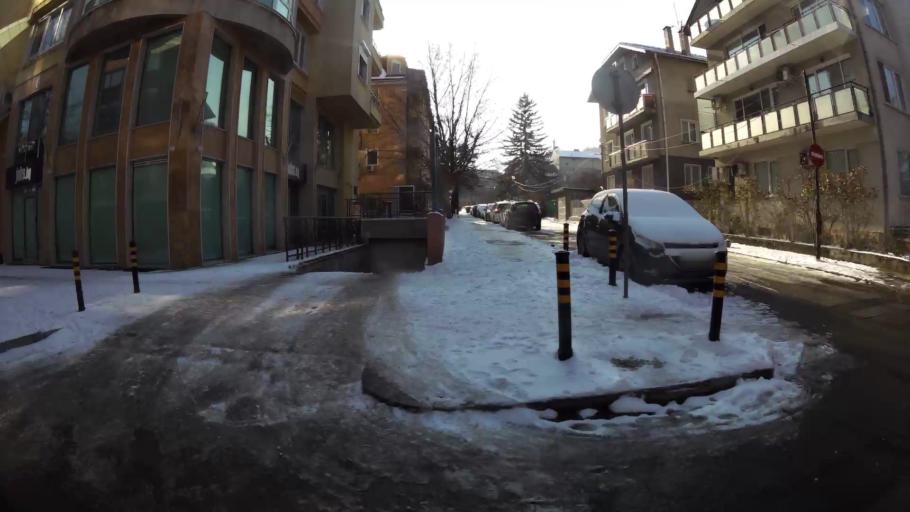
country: BG
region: Sofia-Capital
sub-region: Stolichna Obshtina
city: Sofia
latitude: 42.6738
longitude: 23.3573
